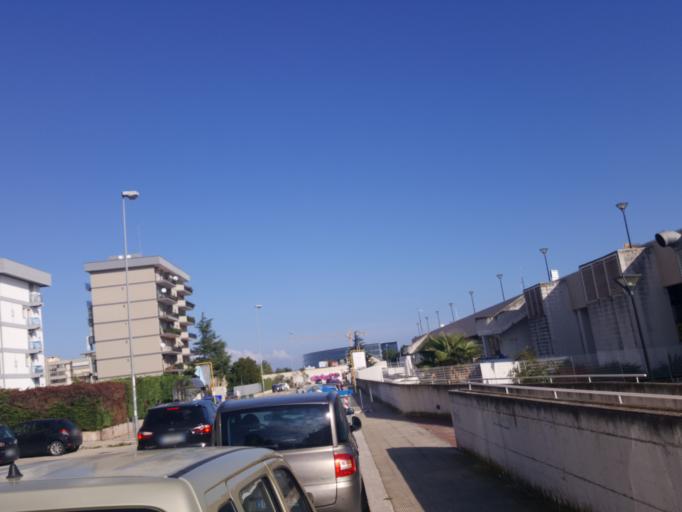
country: IT
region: Apulia
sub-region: Provincia di Bari
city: Triggiano
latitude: 41.1049
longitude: 16.9103
